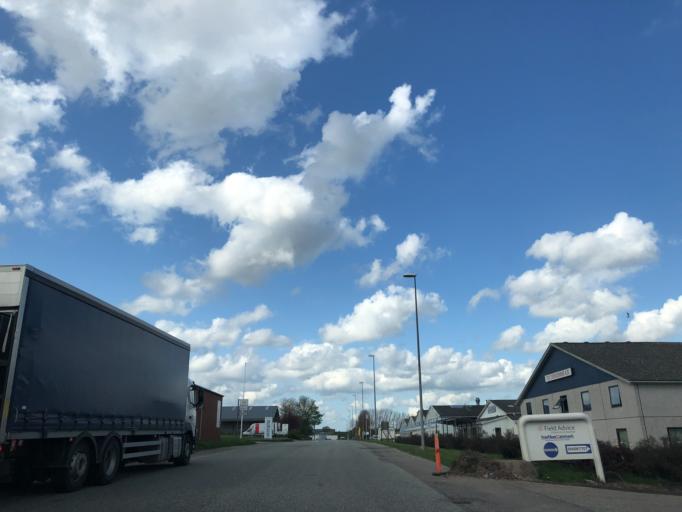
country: DK
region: Zealand
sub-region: Ringsted Kommune
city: Ringsted
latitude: 55.4252
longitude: 11.7896
